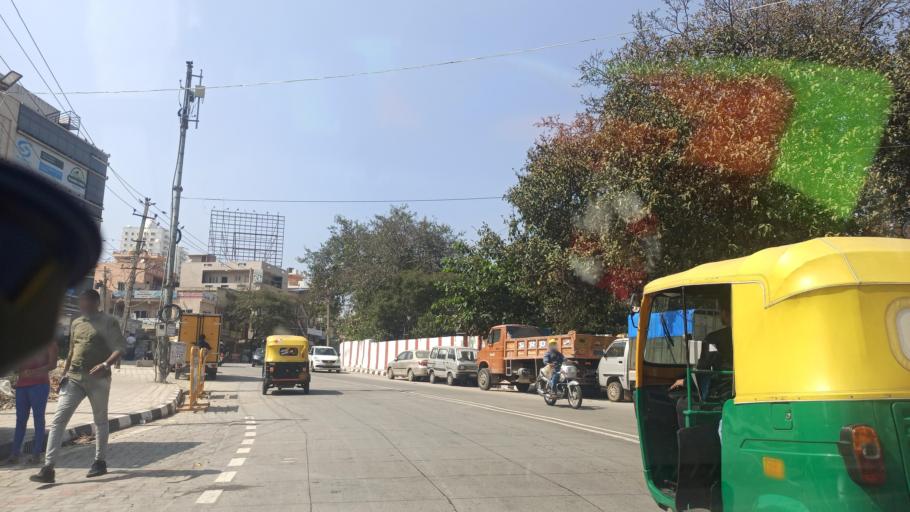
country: IN
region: Karnataka
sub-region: Bangalore Urban
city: Yelahanka
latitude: 13.0576
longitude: 77.5914
